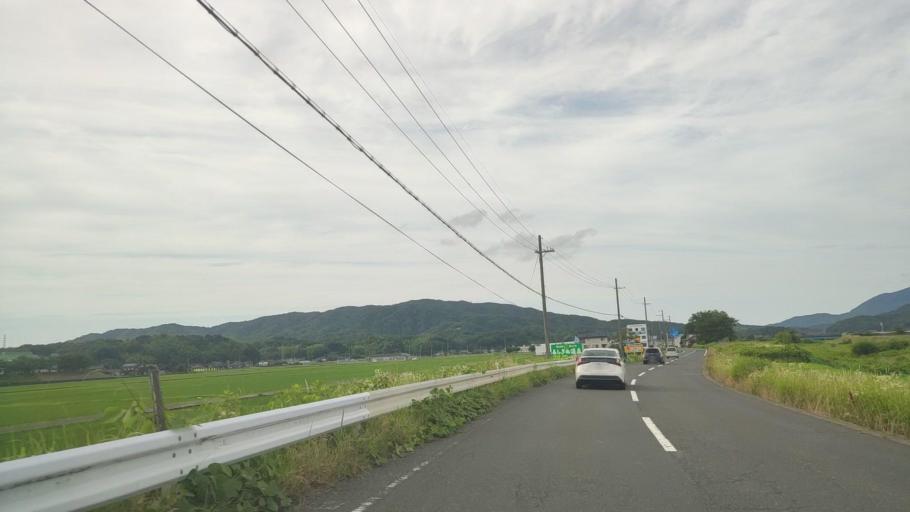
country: JP
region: Kyoto
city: Miyazu
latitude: 35.6652
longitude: 135.0858
